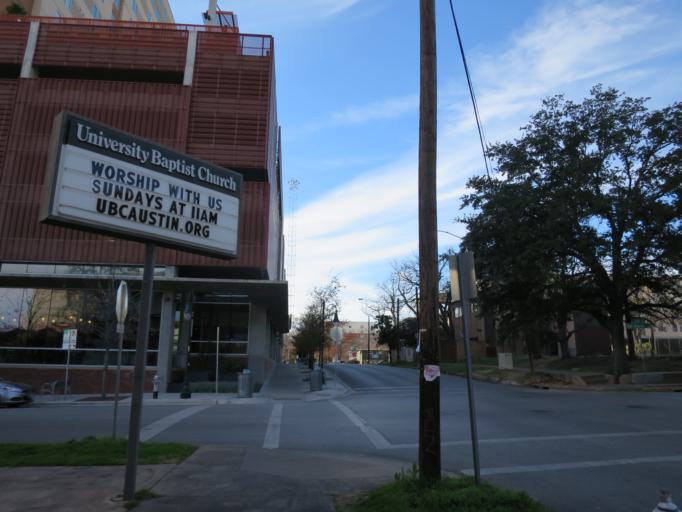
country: US
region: Texas
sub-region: Travis County
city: Austin
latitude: 30.2850
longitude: -97.7427
